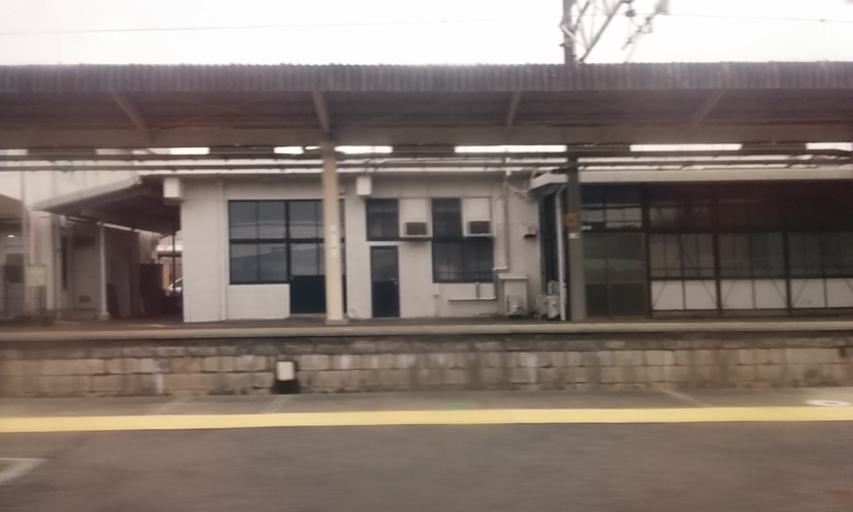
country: JP
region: Gifu
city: Nakatsugawa
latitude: 35.4553
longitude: 137.4080
